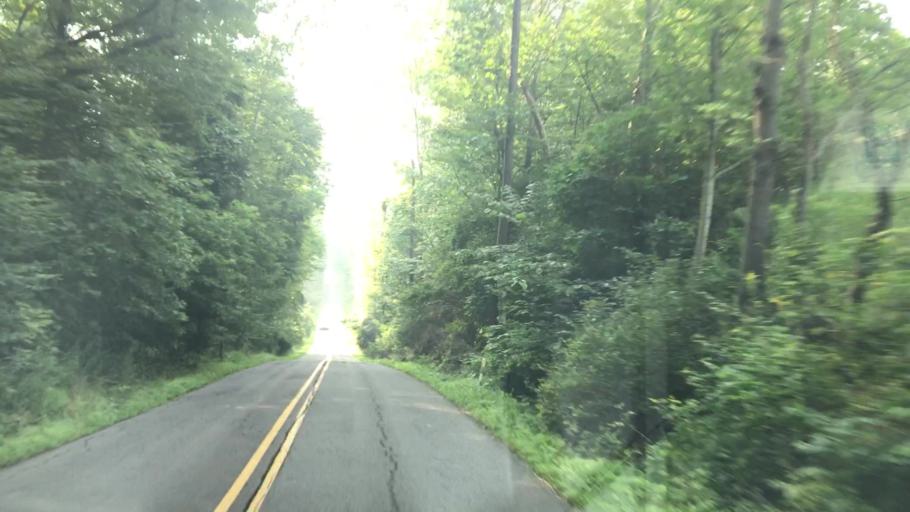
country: US
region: Pennsylvania
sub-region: Wyoming County
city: Factoryville
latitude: 41.6119
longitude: -75.7398
